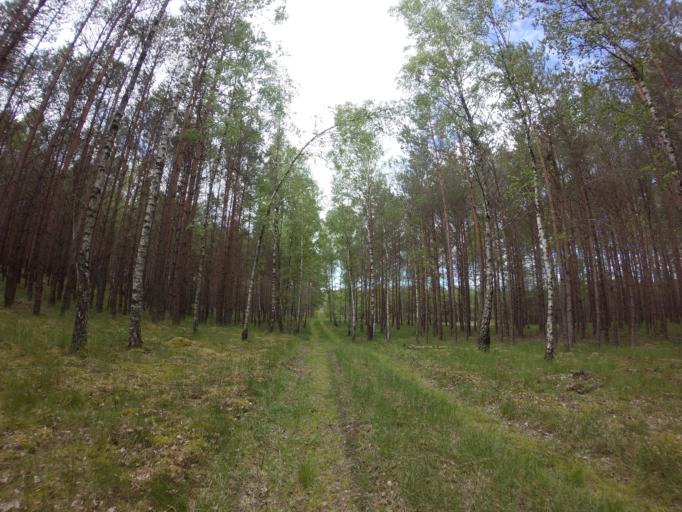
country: PL
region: West Pomeranian Voivodeship
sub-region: Powiat drawski
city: Kalisz Pomorski
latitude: 53.1537
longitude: 15.9682
